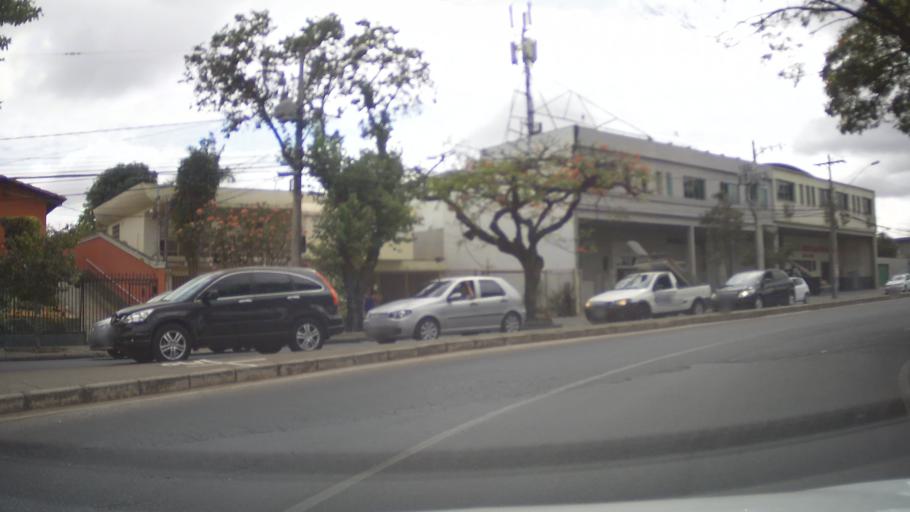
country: BR
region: Minas Gerais
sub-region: Belo Horizonte
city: Belo Horizonte
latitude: -19.8424
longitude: -43.9659
